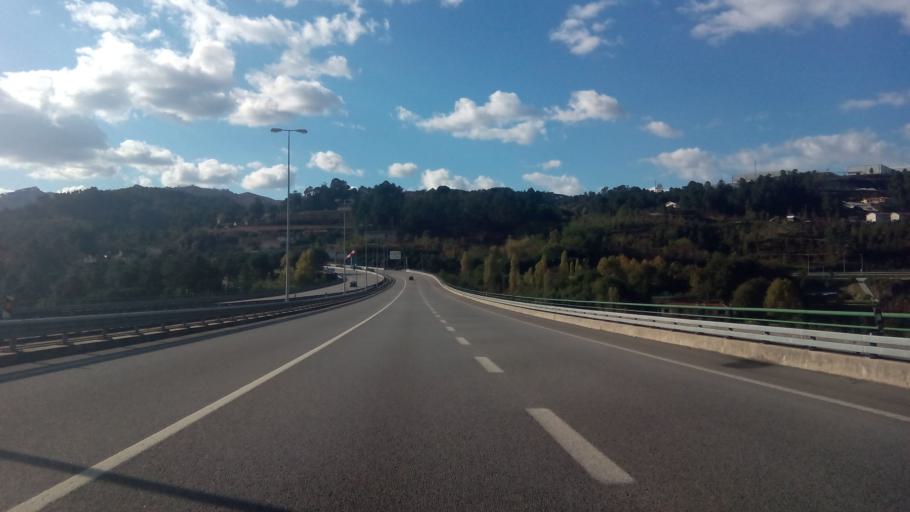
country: PT
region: Porto
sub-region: Amarante
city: Amarante
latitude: 41.2589
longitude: -8.0906
